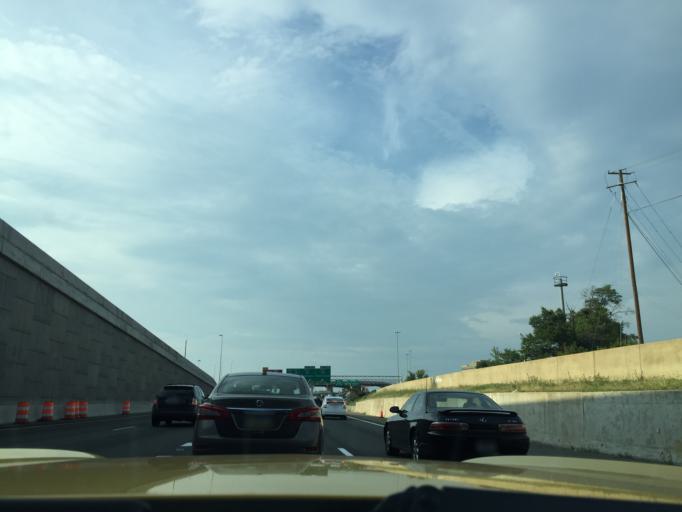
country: US
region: Virginia
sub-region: Fairfax County
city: Springfield
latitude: 38.7704
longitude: -77.1822
